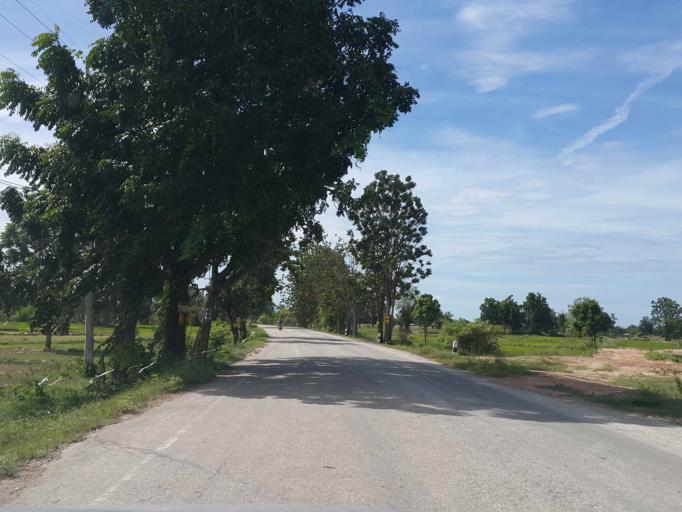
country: TH
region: Sukhothai
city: Ban Dan Lan Hoi
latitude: 17.1383
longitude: 99.5245
